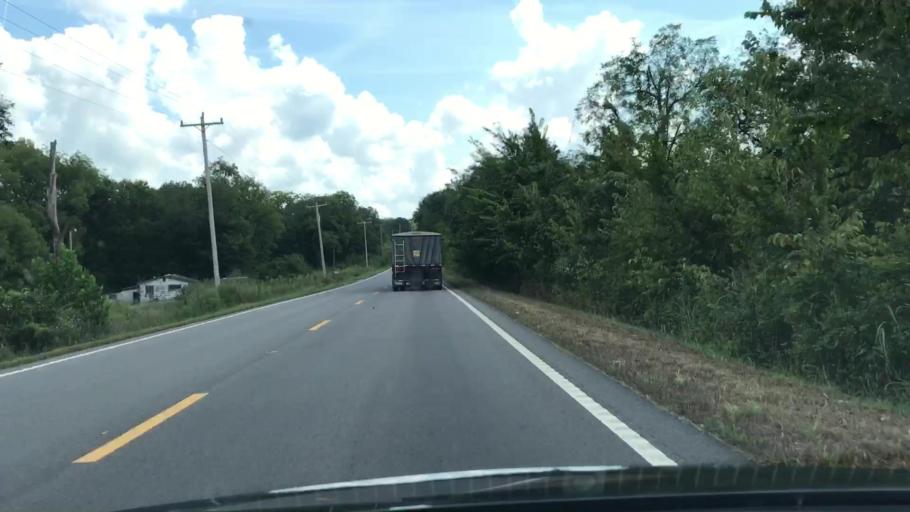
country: US
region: Tennessee
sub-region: Robertson County
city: Springfield
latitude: 36.6313
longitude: -86.9622
